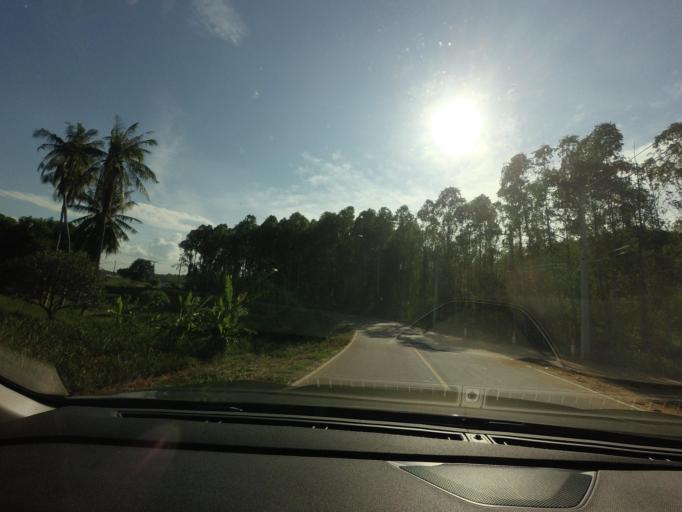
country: TH
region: Prachuap Khiri Khan
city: Pran Buri
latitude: 12.4125
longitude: 99.9665
